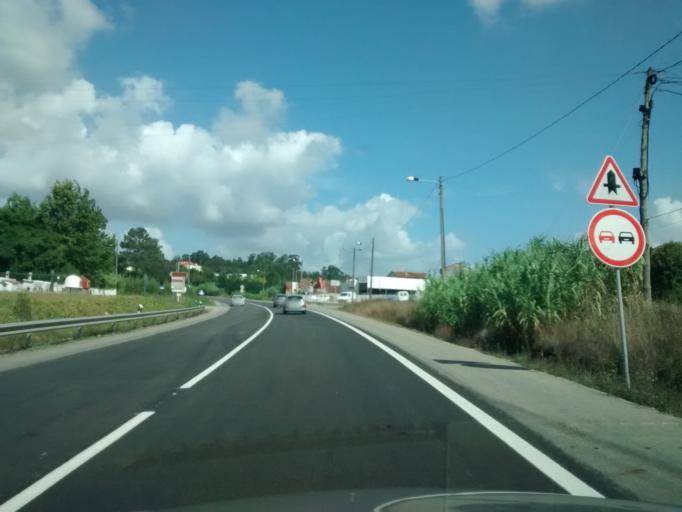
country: PT
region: Aveiro
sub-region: Oliveira do Bairro
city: Oliveira do Bairro
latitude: 40.5334
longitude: -8.5096
